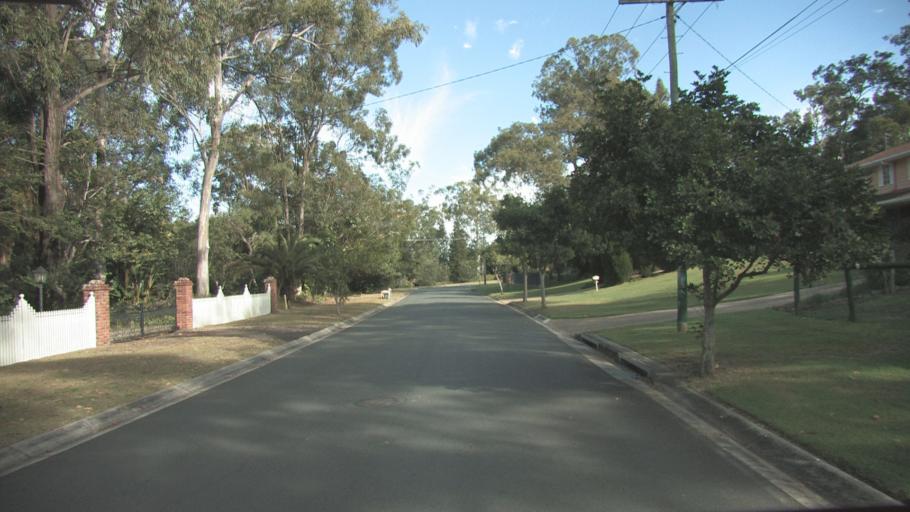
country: AU
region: Queensland
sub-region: Brisbane
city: Forest Lake
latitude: -27.6698
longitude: 153.0109
